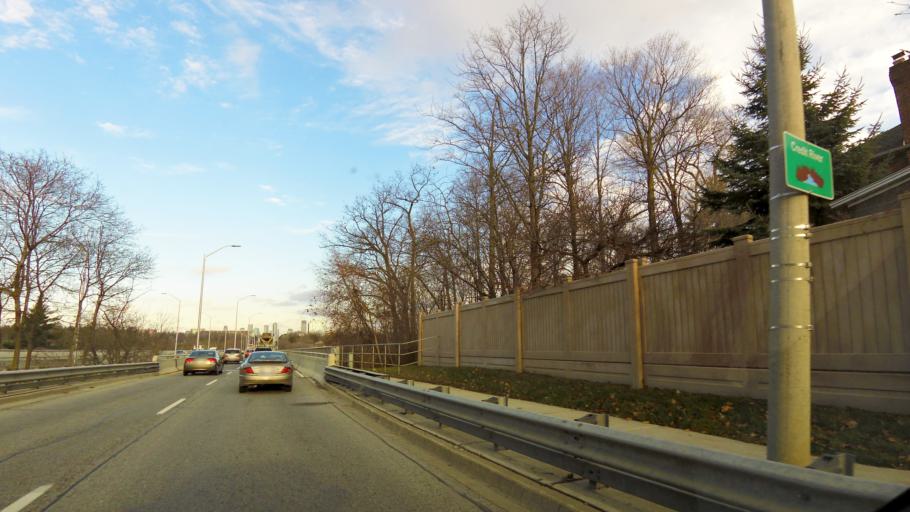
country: CA
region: Ontario
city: Mississauga
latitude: 43.5593
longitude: -79.6744
